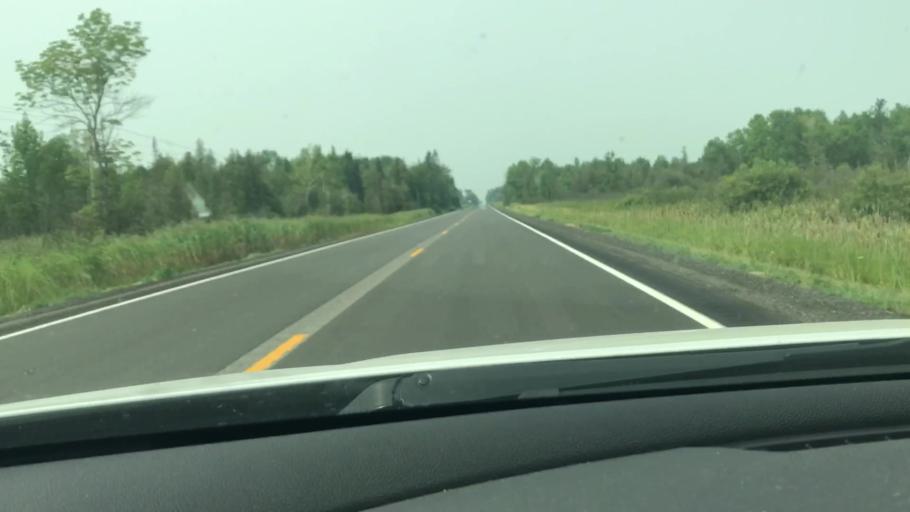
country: US
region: Minnesota
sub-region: Itasca County
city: Cohasset
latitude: 47.3523
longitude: -93.8426
